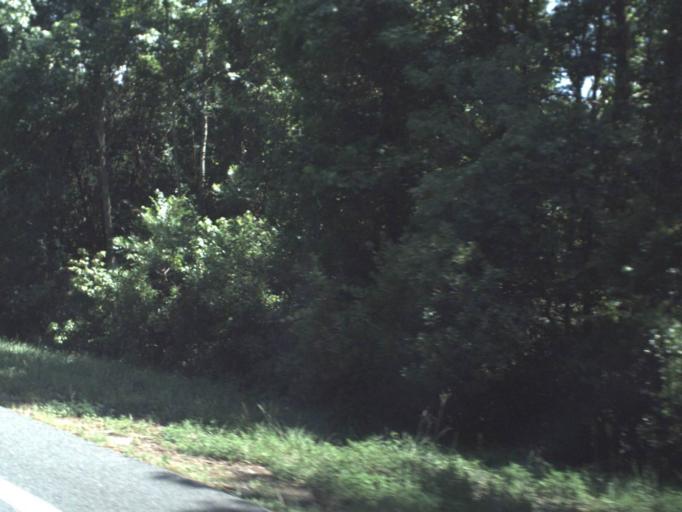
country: US
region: Florida
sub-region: Nassau County
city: Yulee
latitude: 30.6612
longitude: -81.6337
